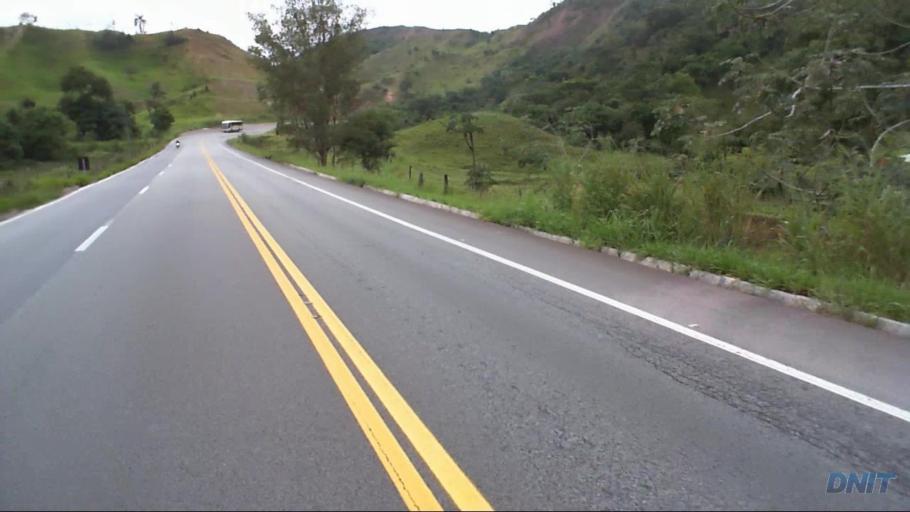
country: BR
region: Minas Gerais
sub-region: Timoteo
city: Timoteo
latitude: -19.6251
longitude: -42.8601
